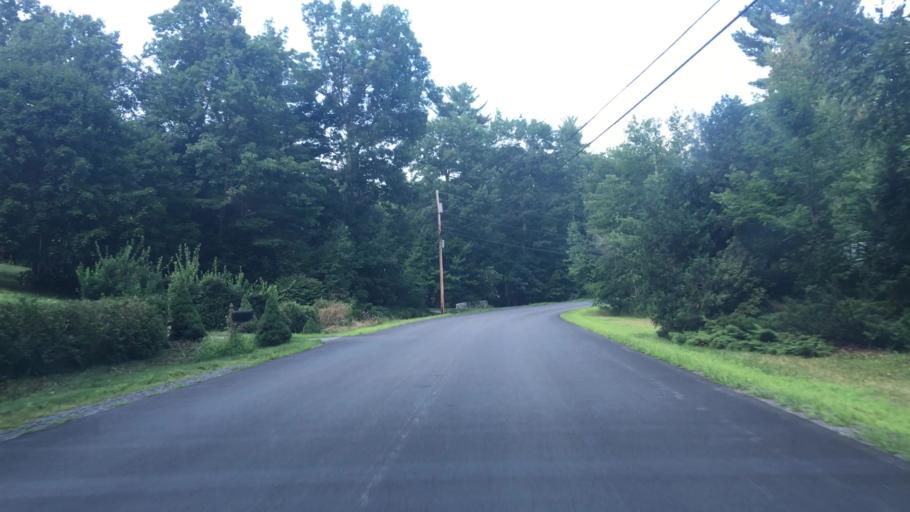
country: US
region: New Hampshire
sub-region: Rockingham County
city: Derry Village
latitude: 42.9386
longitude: -71.3337
